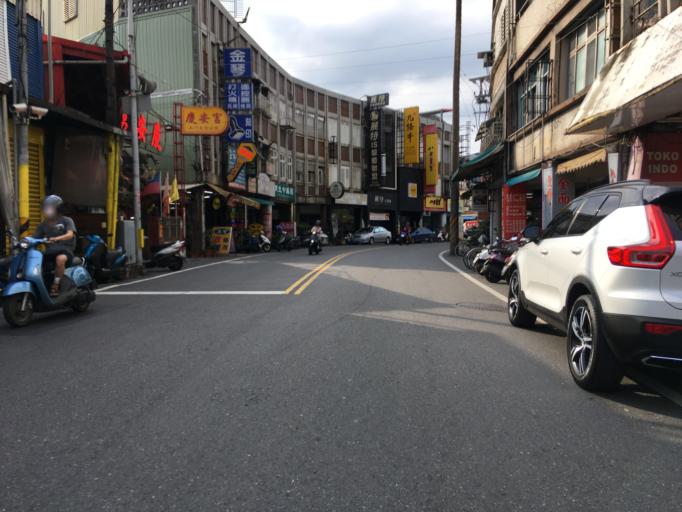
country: TW
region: Taiwan
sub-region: Yilan
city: Yilan
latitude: 24.6720
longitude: 121.7703
